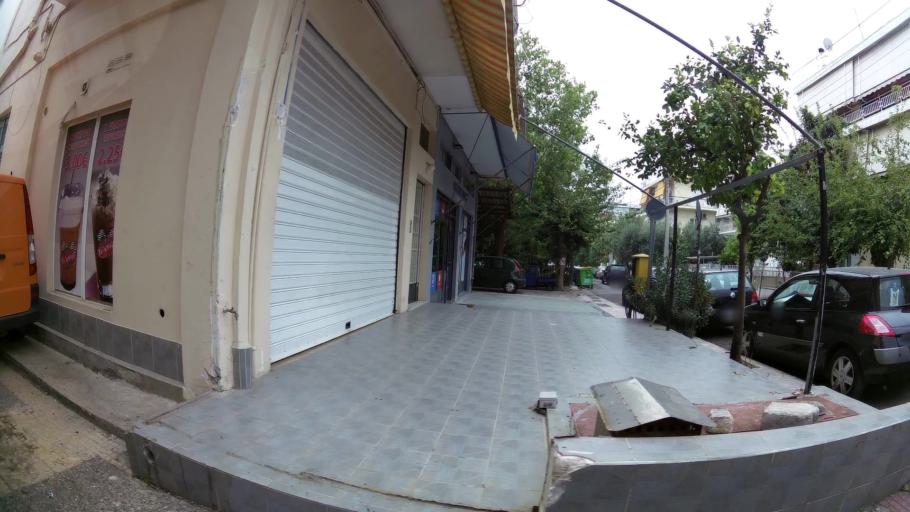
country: GR
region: Attica
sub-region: Nomarchia Athinas
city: Chaidari
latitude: 38.0009
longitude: 23.6647
